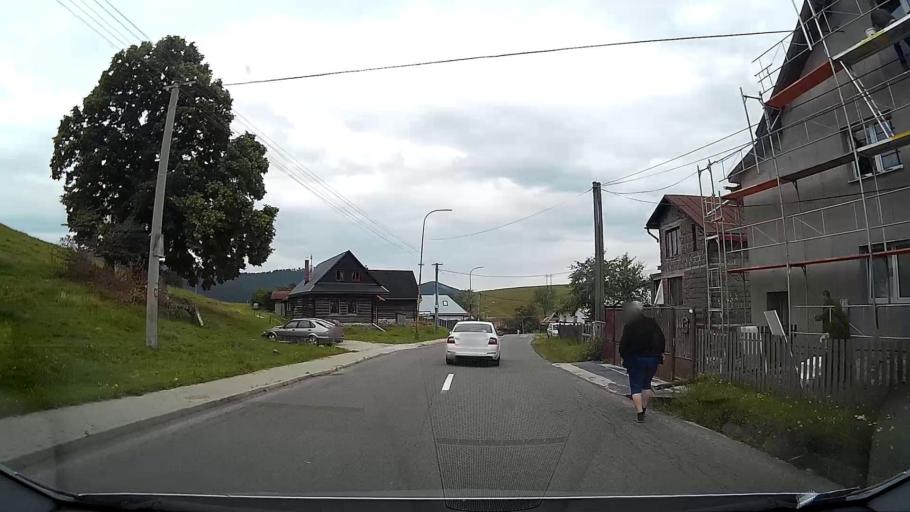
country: SK
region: Banskobystricky
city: Revuca
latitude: 48.8478
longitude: 20.1847
